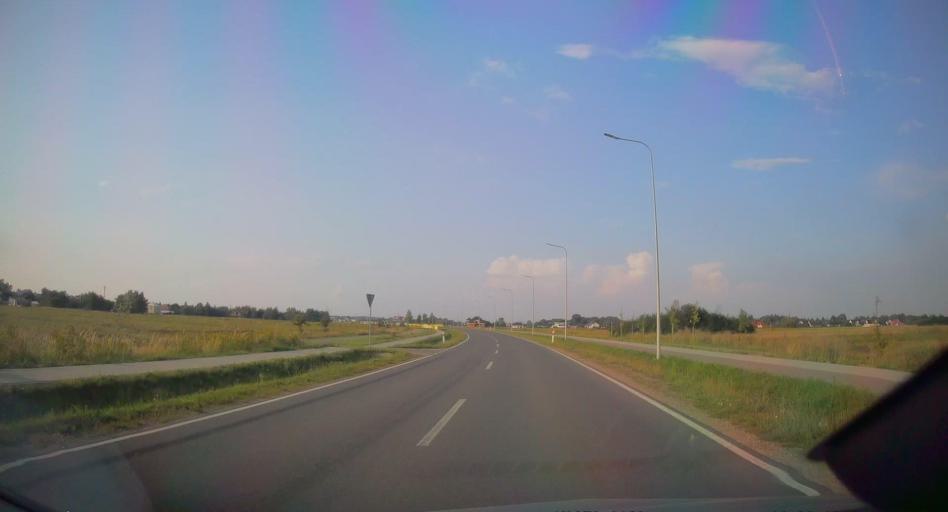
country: PL
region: Subcarpathian Voivodeship
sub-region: Powiat debicki
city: Zyrakow
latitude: 50.0671
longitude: 21.3792
